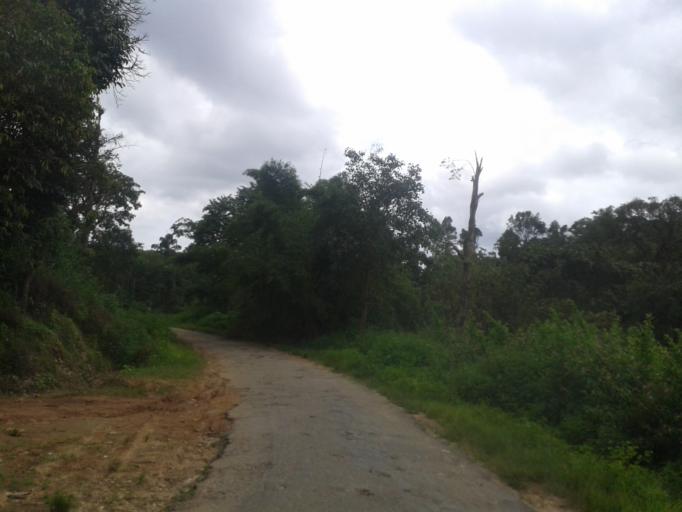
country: IN
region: Karnataka
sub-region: Chikmagalur
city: Mudigere
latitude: 13.0131
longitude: 75.6668
